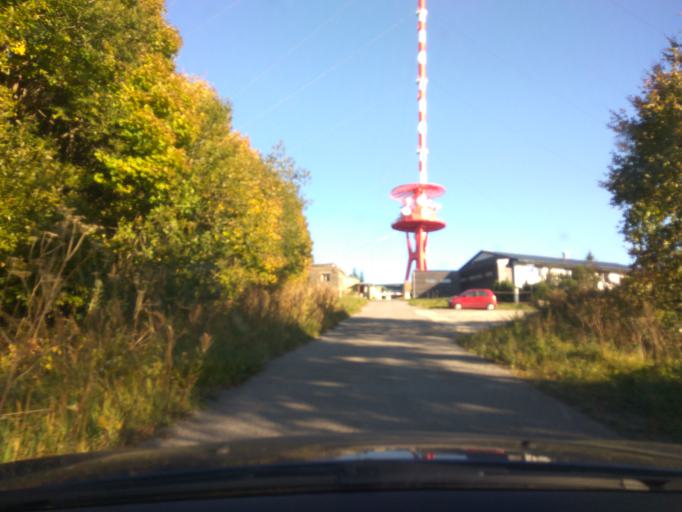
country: SK
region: Banskobystricky
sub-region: Okres Ziar nad Hronom
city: Kremnica
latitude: 48.7395
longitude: 18.9935
